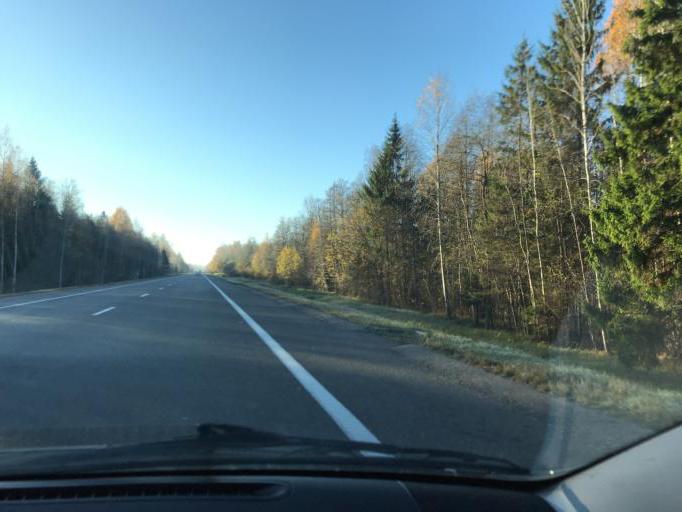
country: BY
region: Vitebsk
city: Vitebsk
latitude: 54.9853
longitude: 30.3441
